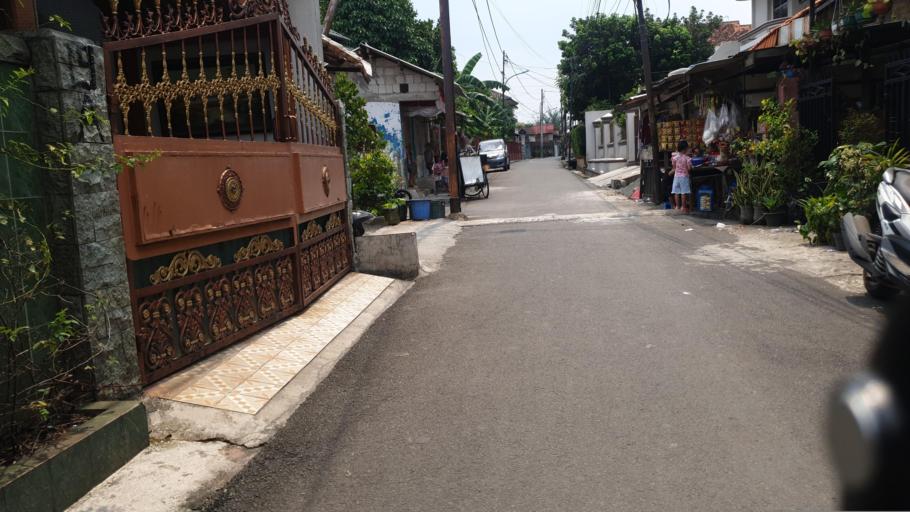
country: ID
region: West Java
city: Ciputat
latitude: -6.1958
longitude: 106.7588
